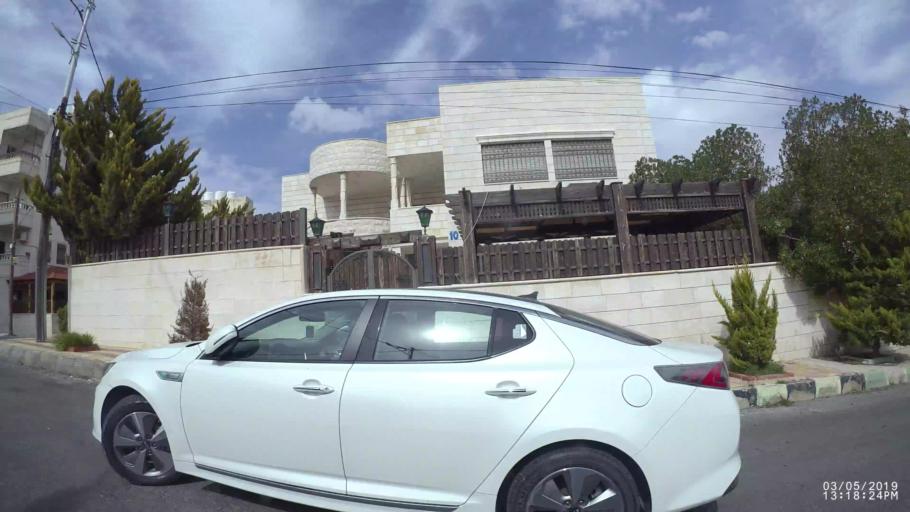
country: JO
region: Amman
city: Amman
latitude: 32.0018
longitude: 35.9341
